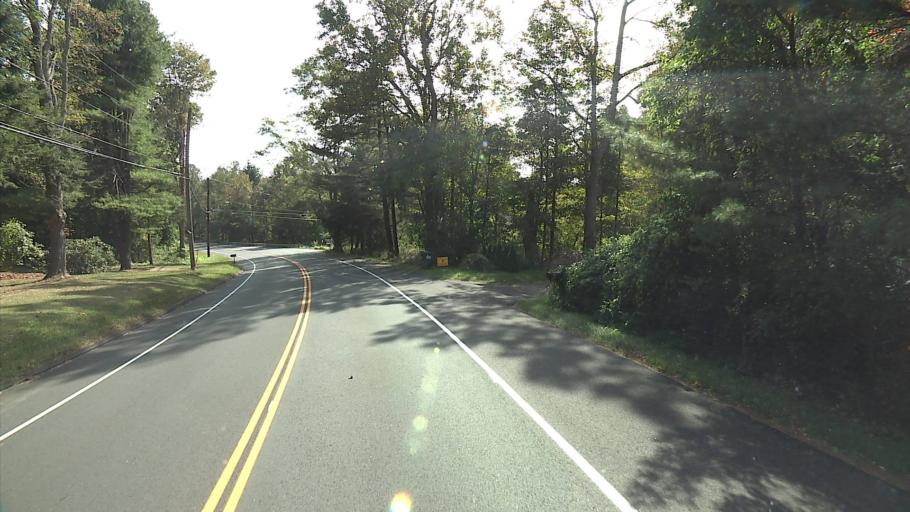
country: US
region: Connecticut
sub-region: New Haven County
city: Southbury
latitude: 41.3855
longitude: -73.2062
